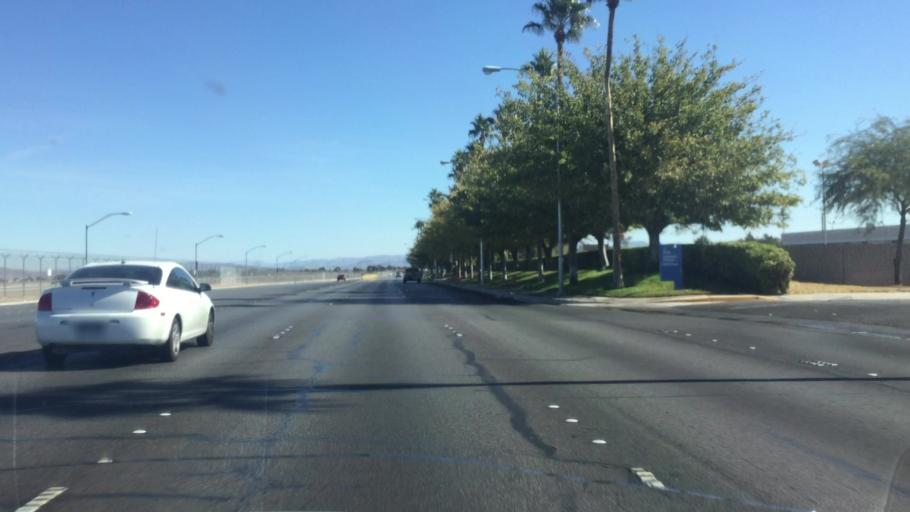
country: US
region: Nevada
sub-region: Clark County
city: Paradise
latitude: 36.0716
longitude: -115.1395
